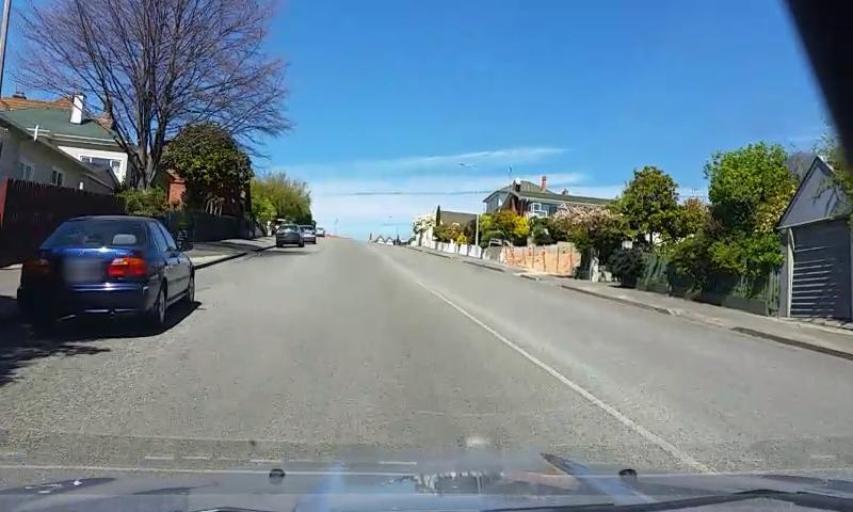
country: NZ
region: Canterbury
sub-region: Timaru District
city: Timaru
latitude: -44.3892
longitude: 171.2406
